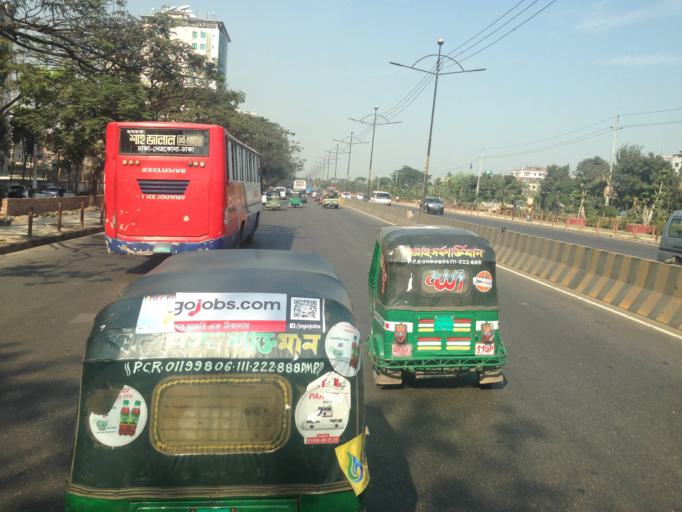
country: BD
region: Dhaka
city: Tungi
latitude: 23.8310
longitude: 90.4195
